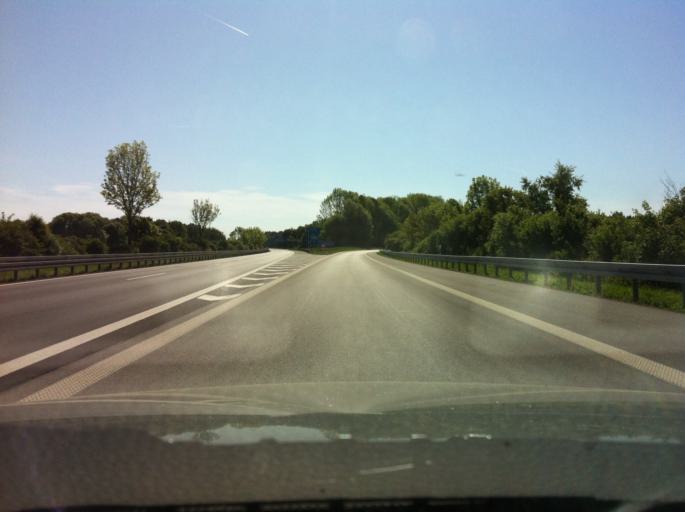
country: DE
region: Bavaria
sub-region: Upper Bavaria
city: Taufkirchen
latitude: 48.0279
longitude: 11.6289
